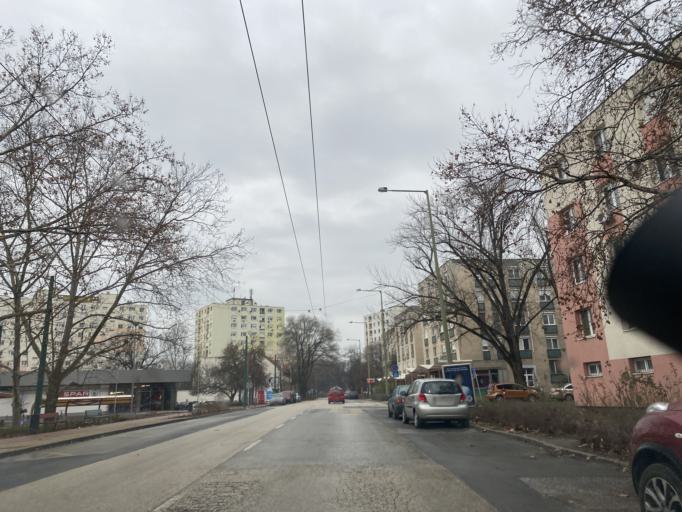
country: HU
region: Csongrad
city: Szeged
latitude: 46.2449
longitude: 20.1600
